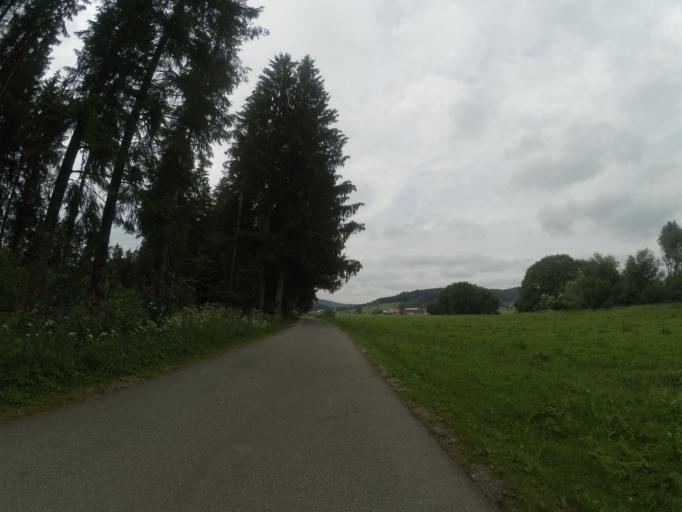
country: DE
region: Baden-Wuerttemberg
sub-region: Tuebingen Region
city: Isny im Allgau
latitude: 47.7123
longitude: 10.0604
